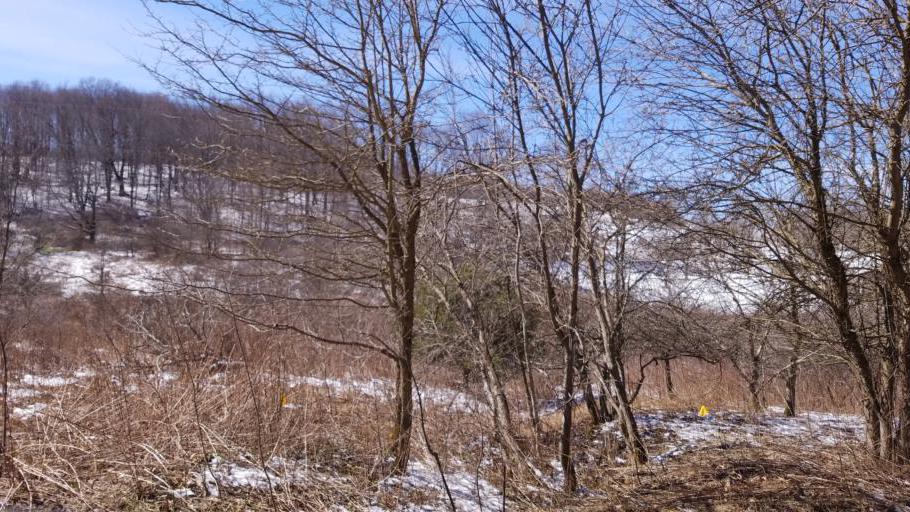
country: US
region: Pennsylvania
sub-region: Tioga County
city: Westfield
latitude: 41.9318
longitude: -77.7320
